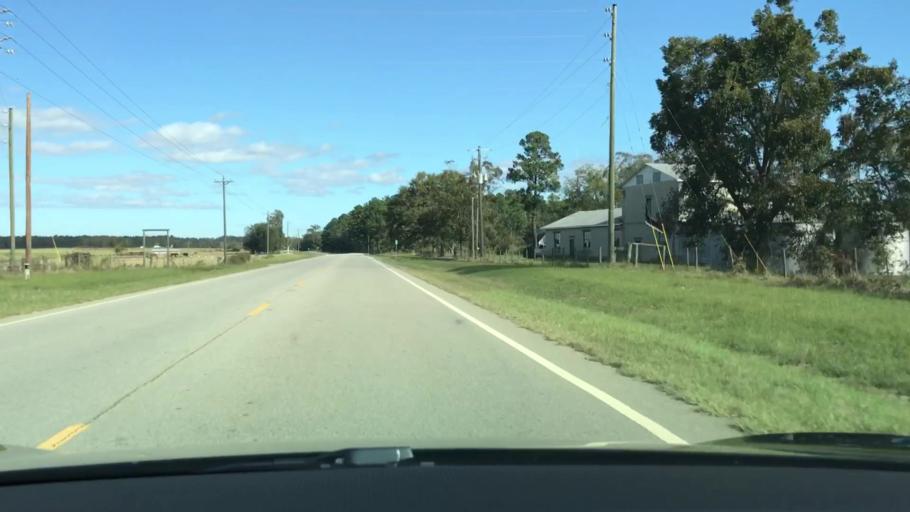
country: US
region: Georgia
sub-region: Jefferson County
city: Wrens
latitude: 33.1700
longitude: -82.4546
